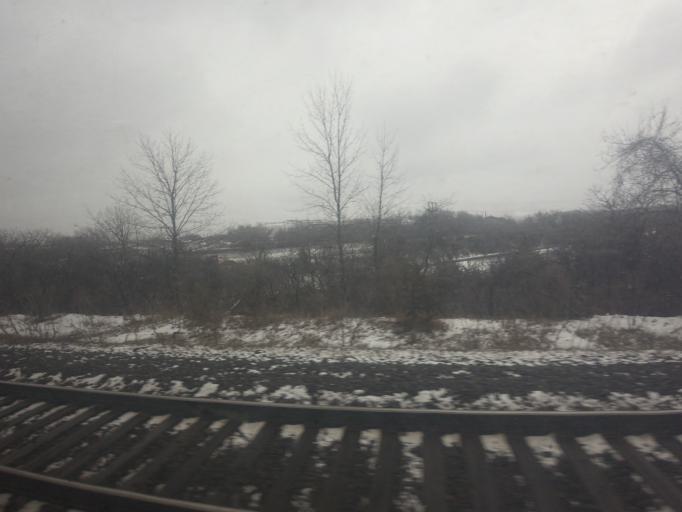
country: CA
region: Ontario
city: Quinte West
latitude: 44.1207
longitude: -77.5923
